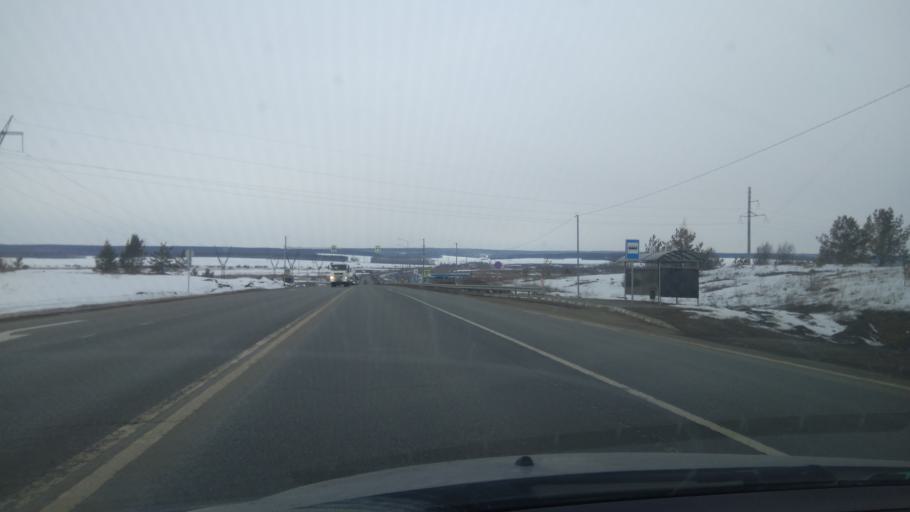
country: RU
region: Sverdlovsk
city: Achit
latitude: 56.7819
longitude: 57.9157
